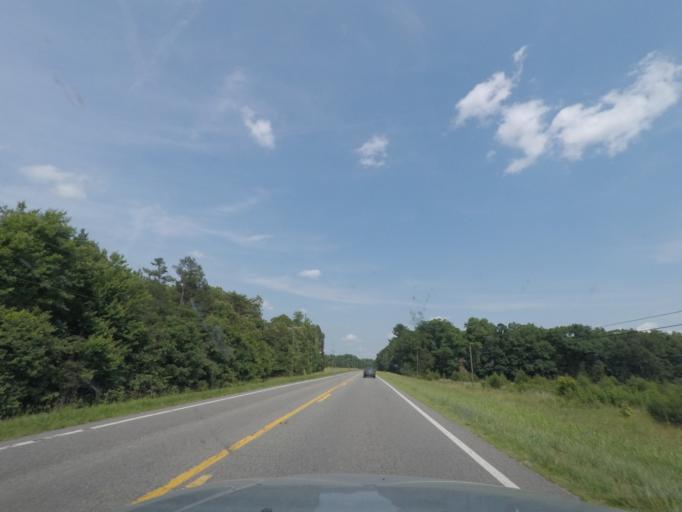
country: US
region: Virginia
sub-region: Fluvanna County
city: Palmyra
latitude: 37.8159
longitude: -78.2569
